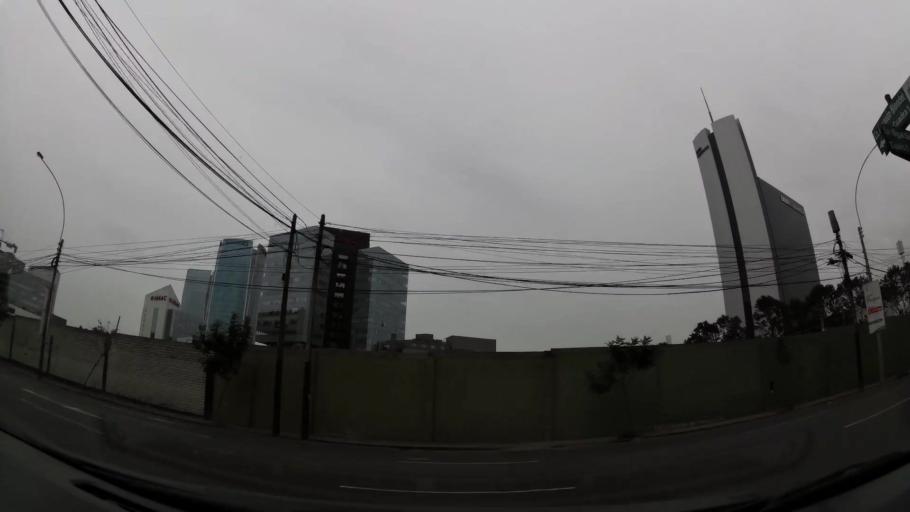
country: PE
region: Lima
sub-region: Lima
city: San Luis
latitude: -12.0948
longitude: -77.0224
